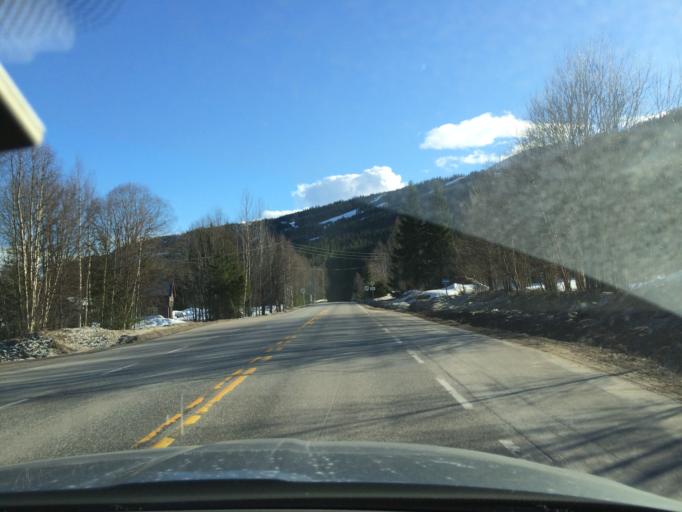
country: NO
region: Hedmark
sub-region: Trysil
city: Innbygda
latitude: 61.3403
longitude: 12.2198
